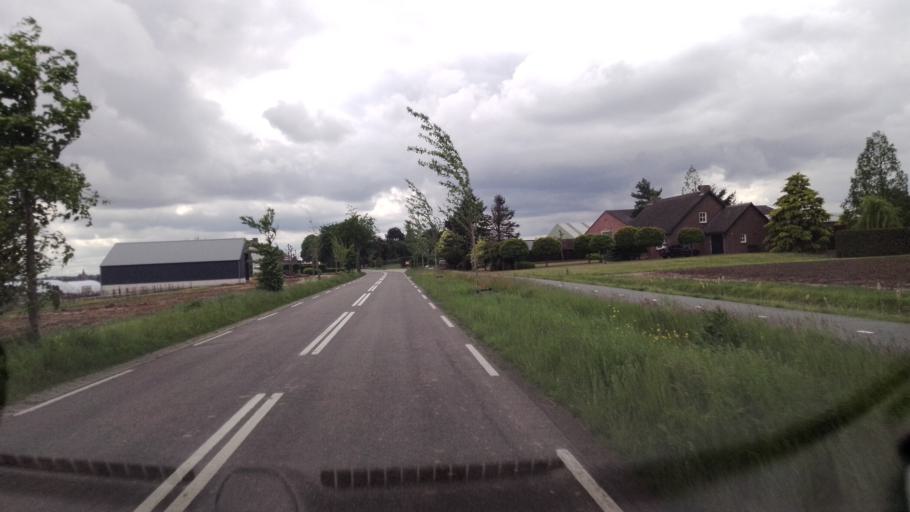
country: NL
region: Limburg
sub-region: Gemeente Venlo
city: Arcen
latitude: 51.4377
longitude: 6.1483
